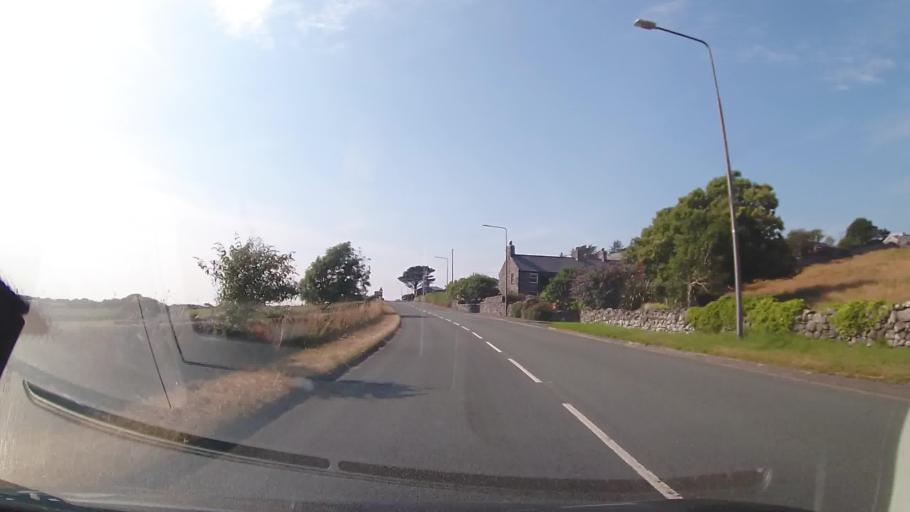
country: GB
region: Wales
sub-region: Gwynedd
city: Llanfair
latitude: 52.8417
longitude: -4.1159
